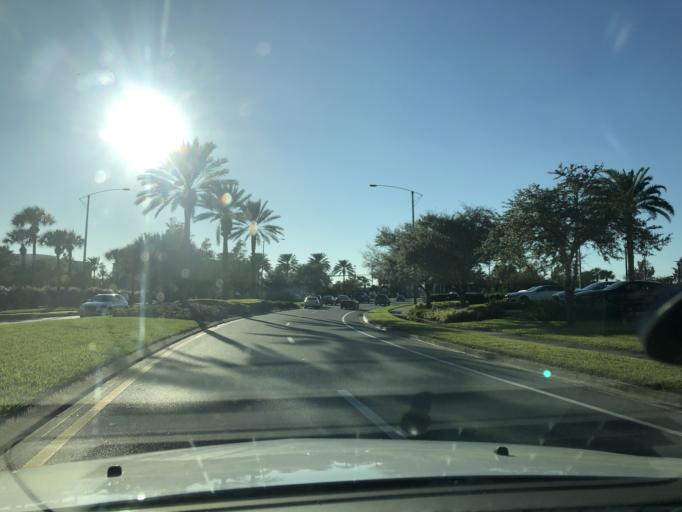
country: US
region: Florida
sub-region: Orange County
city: Oak Ridge
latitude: 28.4886
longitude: -81.4336
